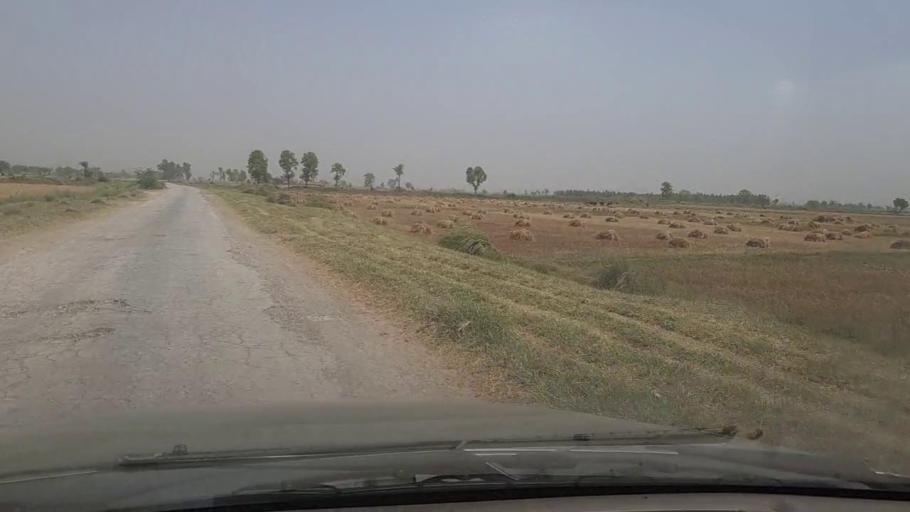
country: PK
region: Sindh
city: Madeji
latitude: 27.8153
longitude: 68.3979
